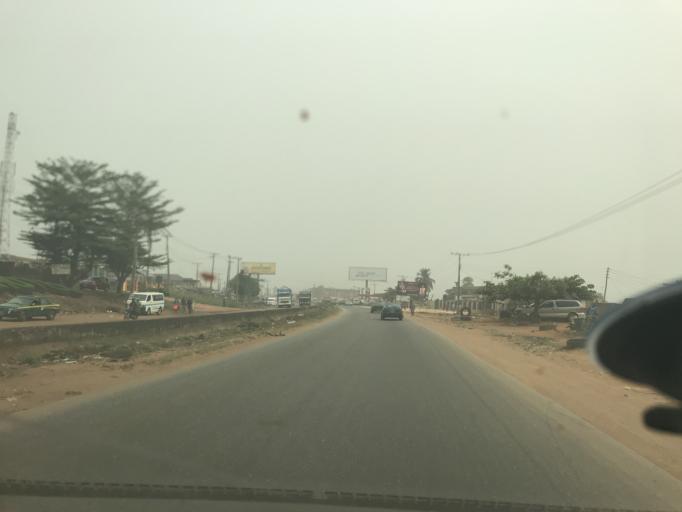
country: NG
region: Ogun
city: Shagamu
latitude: 6.8576
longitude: 3.6274
